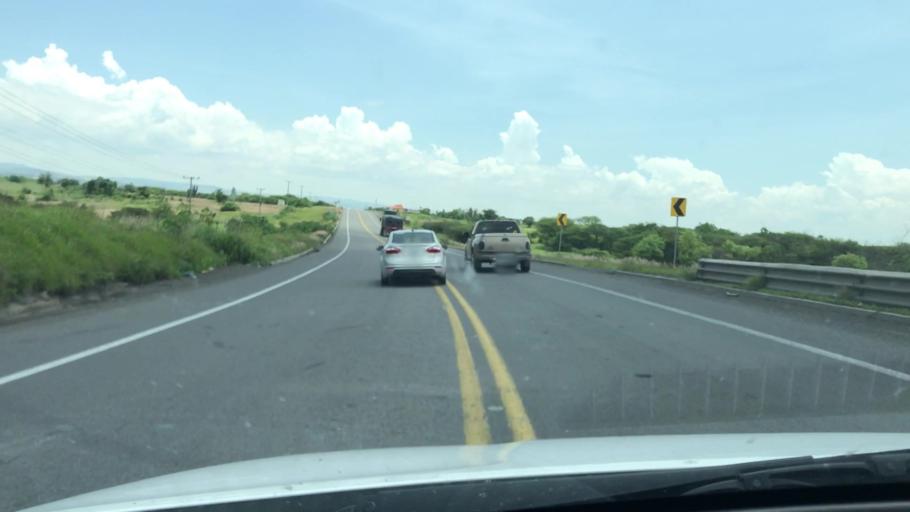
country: MX
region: Michoacan
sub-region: Yurecuaro
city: Yurecuaro
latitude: 20.3436
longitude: -102.1611
